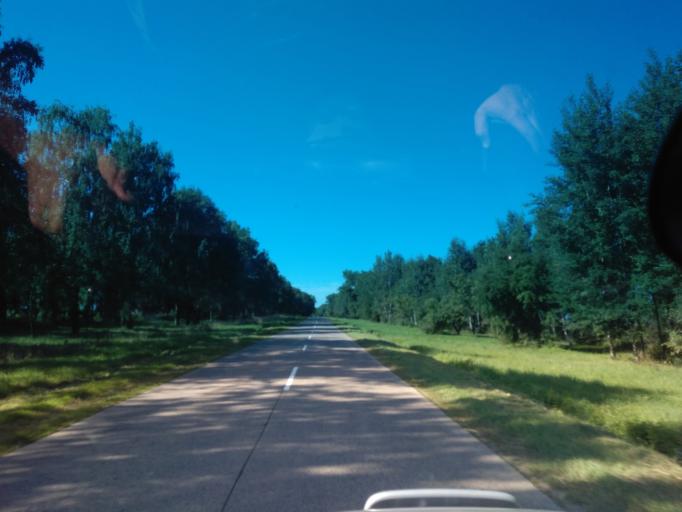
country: BY
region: Minsk
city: Stan'kava
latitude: 53.6470
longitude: 27.3006
